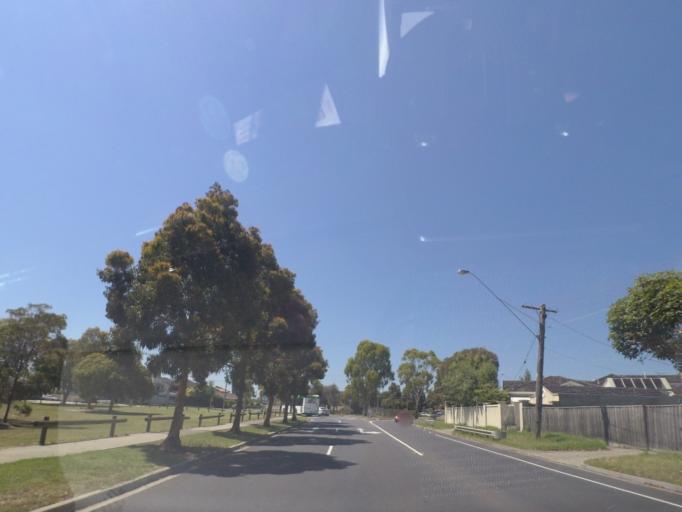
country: AU
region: Victoria
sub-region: Darebin
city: Reservoir
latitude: -37.6969
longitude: 144.9907
